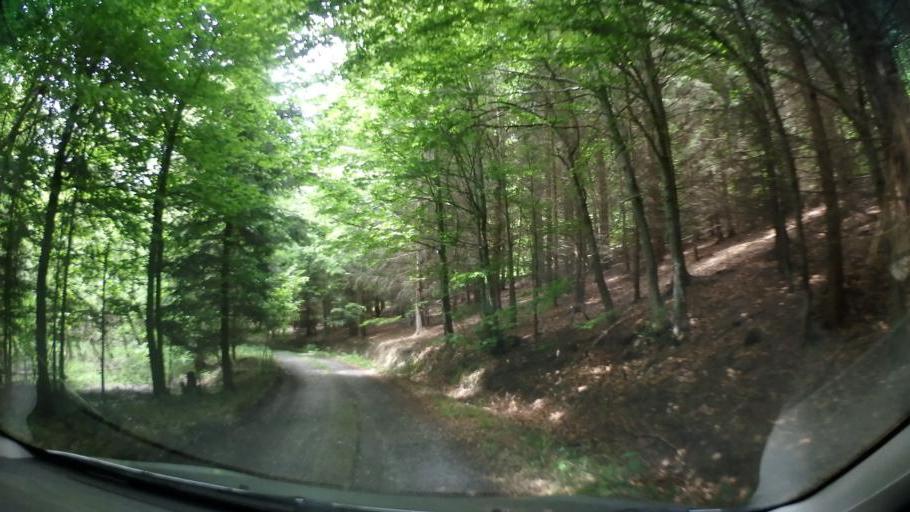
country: CZ
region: Olomoucky
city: Stity
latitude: 49.8730
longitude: 16.7410
